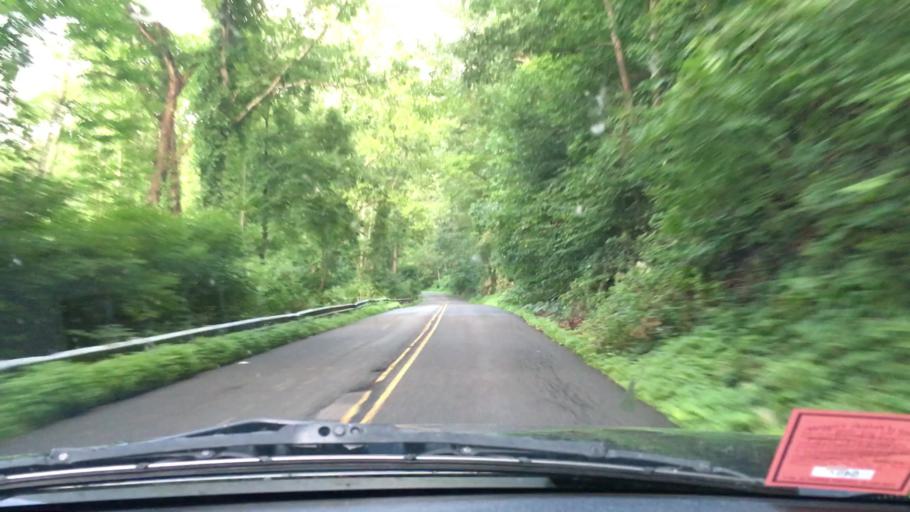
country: US
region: Virginia
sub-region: Pulaski County
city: Pulaski
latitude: 37.0415
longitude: -80.7443
